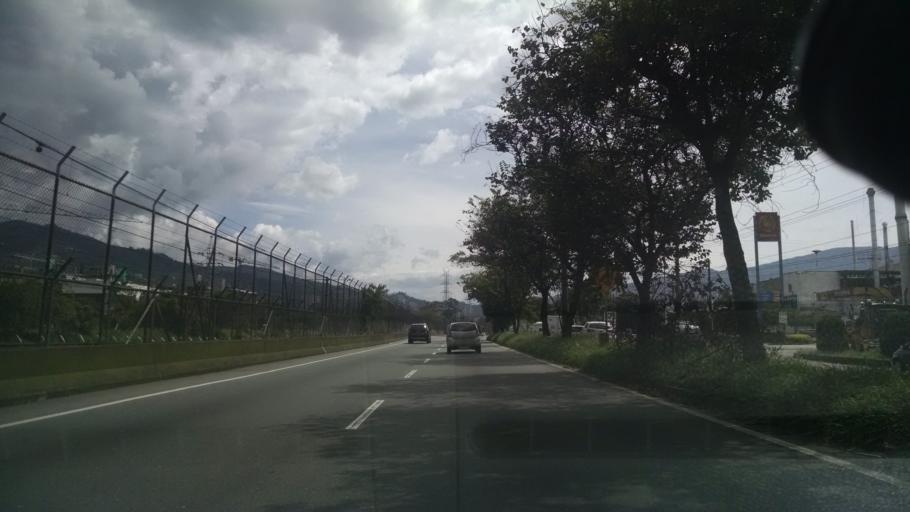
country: CO
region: Antioquia
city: Envigado
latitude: 6.1804
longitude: -75.5915
